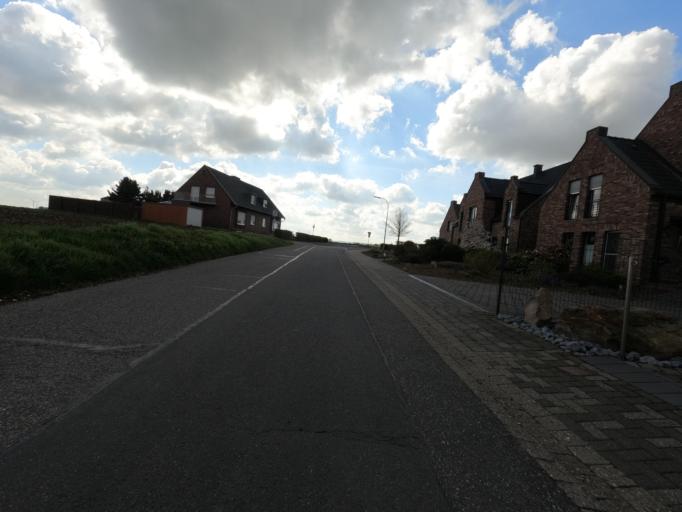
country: DE
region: North Rhine-Westphalia
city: Erkelenz
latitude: 51.0304
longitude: 6.3575
